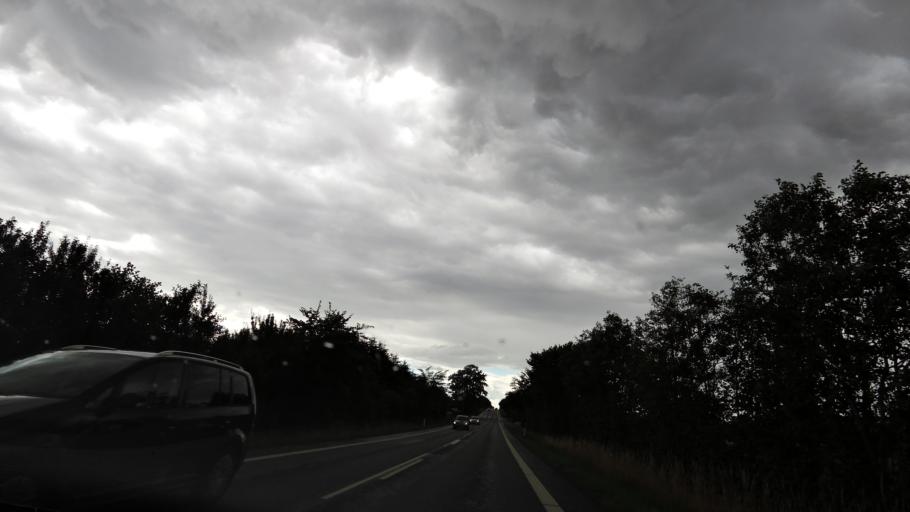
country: DK
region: South Denmark
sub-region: Middelfart Kommune
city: Brenderup
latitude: 55.4505
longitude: 9.9734
